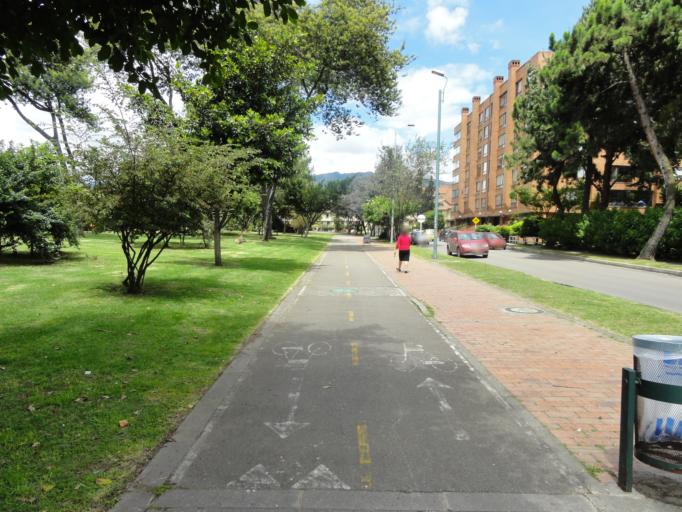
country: CO
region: Bogota D.C.
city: Barrio San Luis
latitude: 4.6982
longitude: -74.0651
